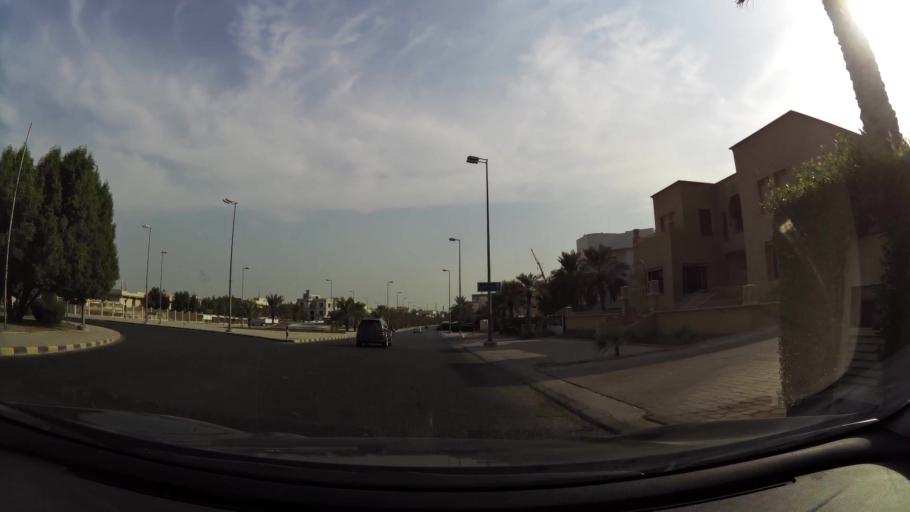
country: KW
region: Al Asimah
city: Ash Shamiyah
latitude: 29.3259
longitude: 47.9811
